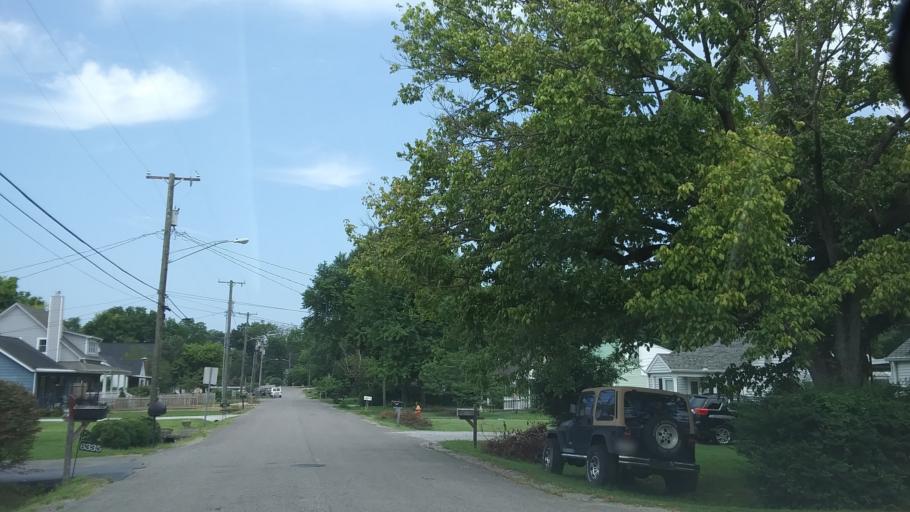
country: US
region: Tennessee
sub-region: Davidson County
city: Belle Meade
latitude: 36.1518
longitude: -86.8707
